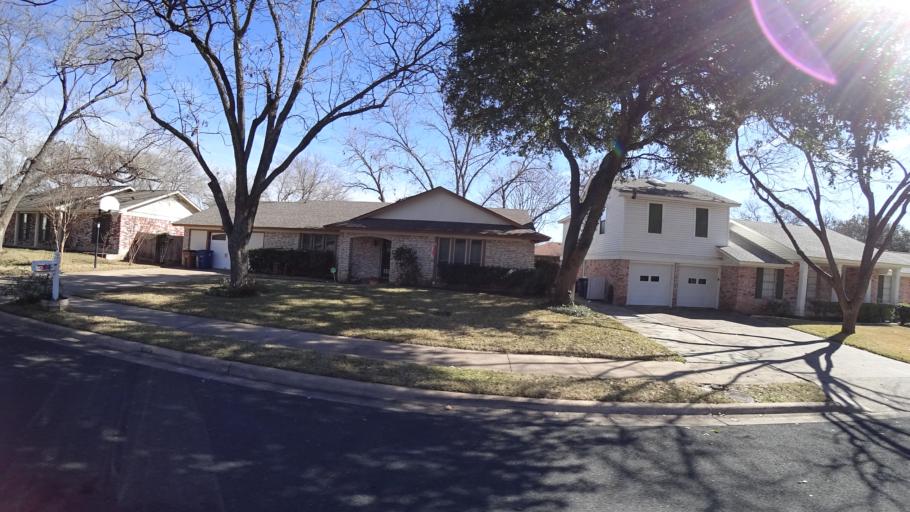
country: US
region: Texas
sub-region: Travis County
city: Wells Branch
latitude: 30.3794
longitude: -97.7012
